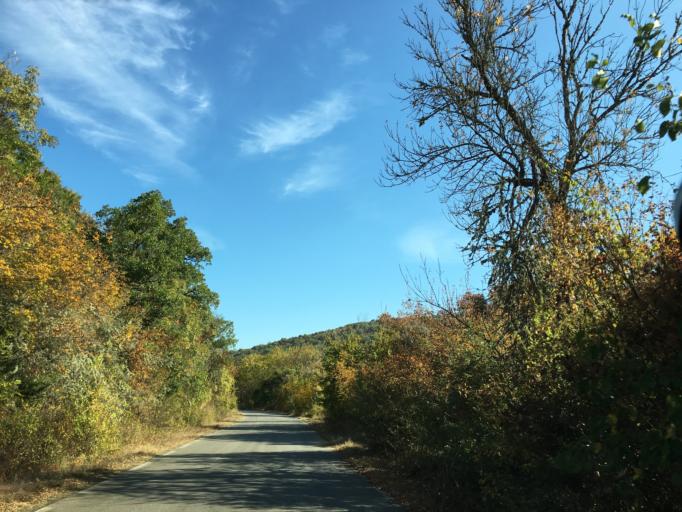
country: BG
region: Khaskovo
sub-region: Obshtina Ivaylovgrad
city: Ivaylovgrad
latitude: 41.4185
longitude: 26.1230
